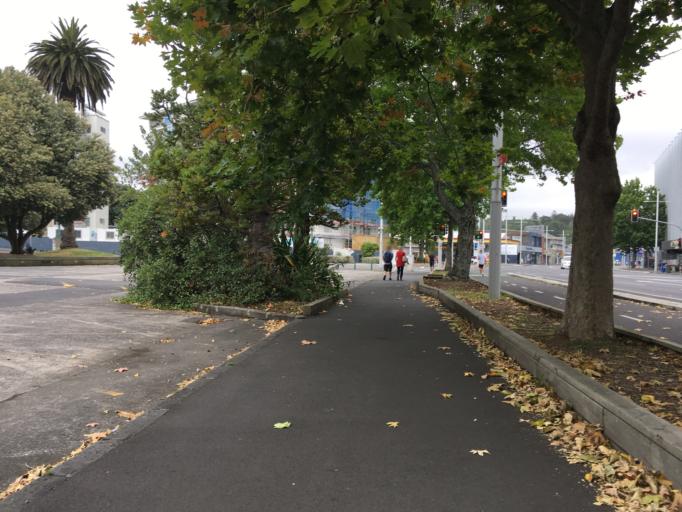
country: NZ
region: Auckland
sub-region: Auckland
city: Auckland
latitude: -36.8483
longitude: 174.7744
